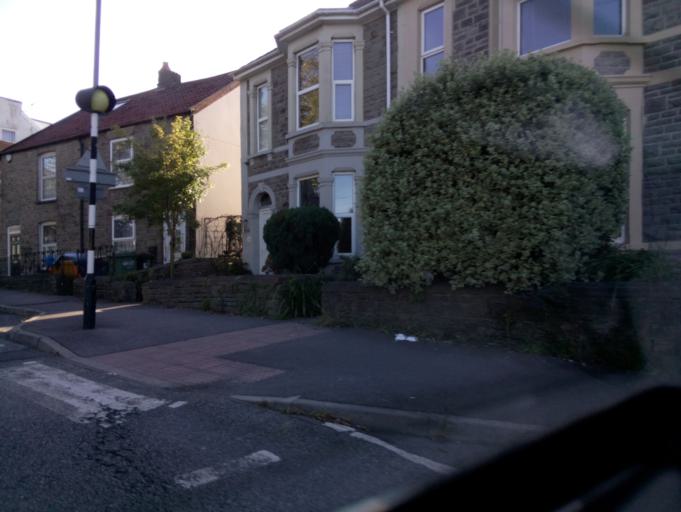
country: GB
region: England
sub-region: South Gloucestershire
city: Mangotsfield
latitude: 51.4801
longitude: -2.5070
